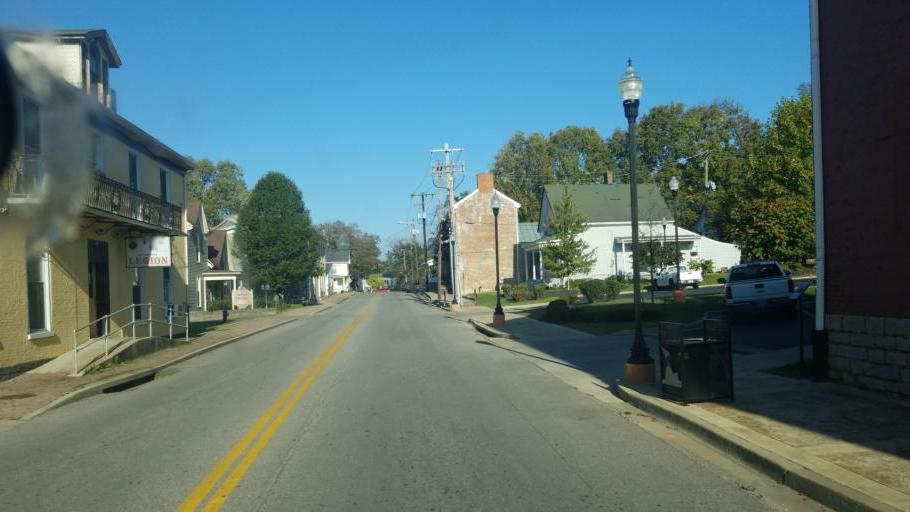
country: US
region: Kentucky
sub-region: Fleming County
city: Flemingsburg
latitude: 38.4226
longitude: -83.7344
